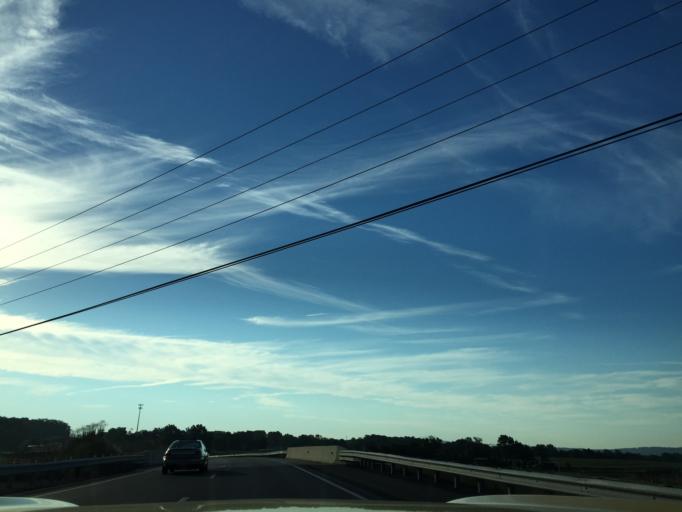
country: US
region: Pennsylvania
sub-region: Lehigh County
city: Ancient Oaks
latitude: 40.5642
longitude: -75.5873
